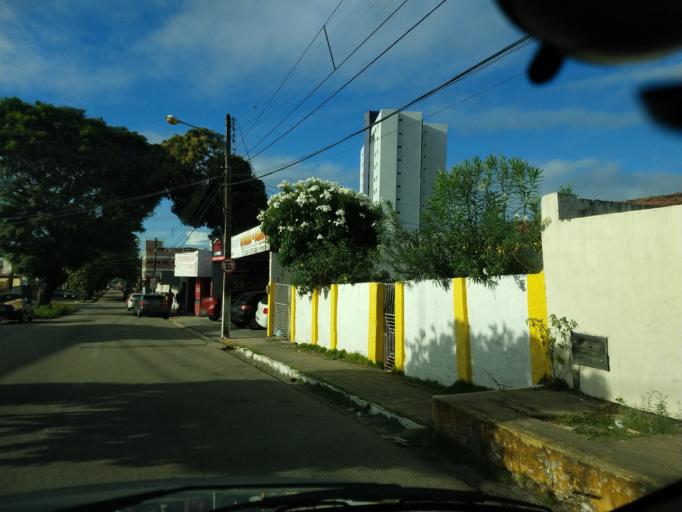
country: BR
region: Rio Grande do Norte
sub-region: Natal
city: Natal
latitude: -5.8052
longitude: -35.2133
